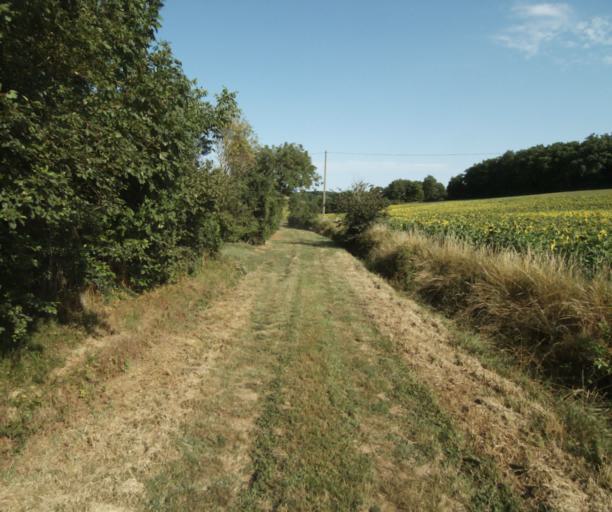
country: FR
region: Midi-Pyrenees
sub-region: Departement de la Haute-Garonne
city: Avignonet-Lauragais
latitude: 43.4159
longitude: 1.8097
